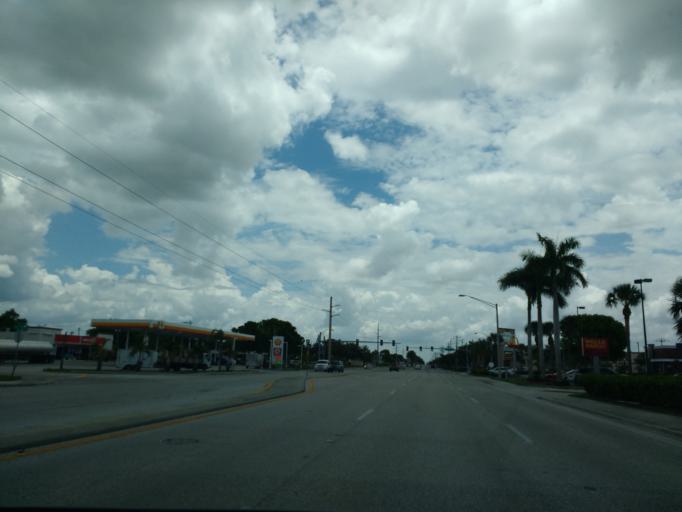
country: US
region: Florida
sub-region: Lee County
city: Cape Coral
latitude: 26.5627
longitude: -82.0081
